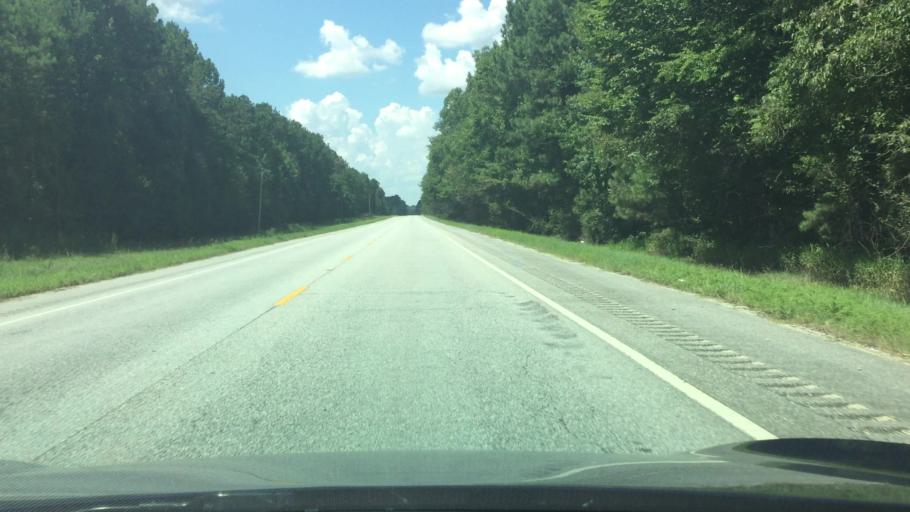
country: US
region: Alabama
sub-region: Montgomery County
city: Pike Road
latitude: 32.3880
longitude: -85.9823
